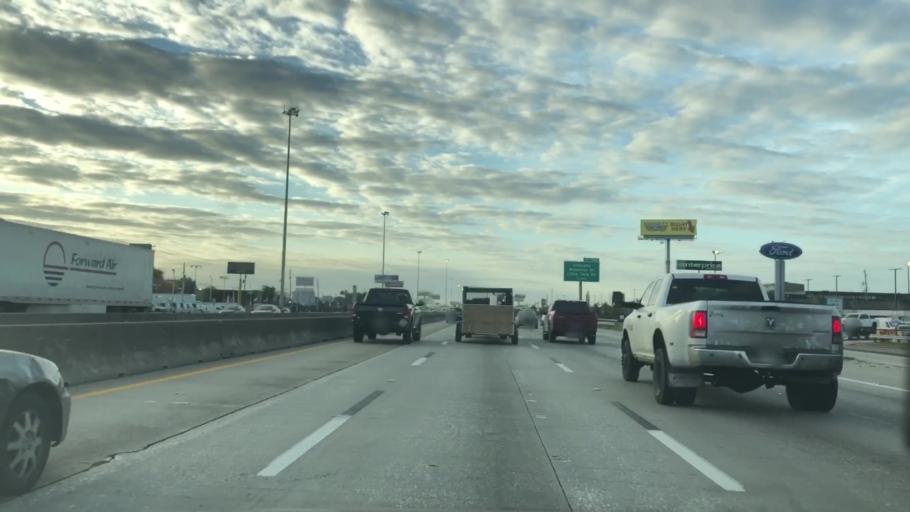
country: US
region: Texas
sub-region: Harris County
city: Aldine
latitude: 29.8954
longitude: -95.4123
